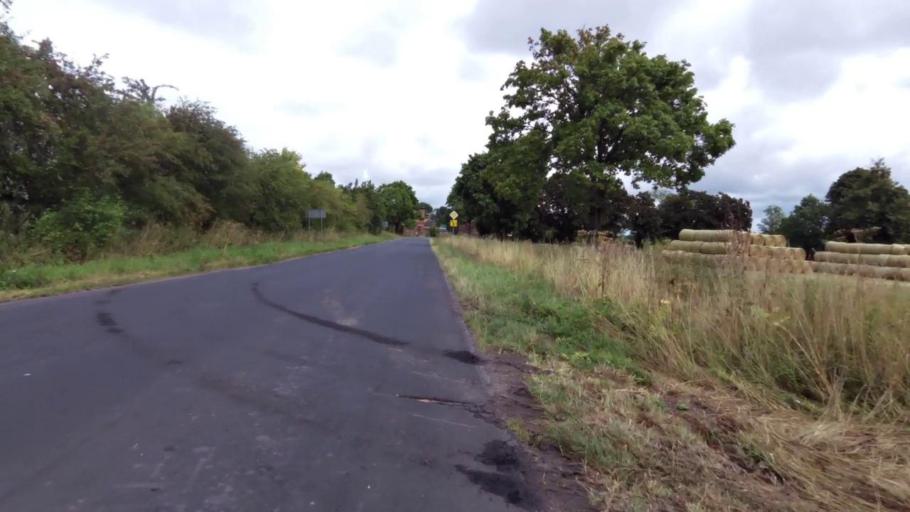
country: PL
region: West Pomeranian Voivodeship
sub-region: Powiat mysliborski
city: Debno
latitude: 52.8461
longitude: 14.6739
